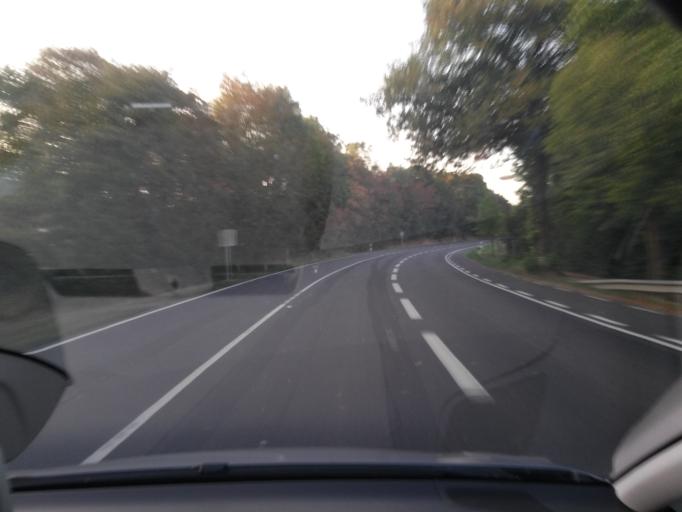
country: LU
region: Luxembourg
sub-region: Canton de Luxembourg
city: Alzingen
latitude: 49.5442
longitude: 6.1741
